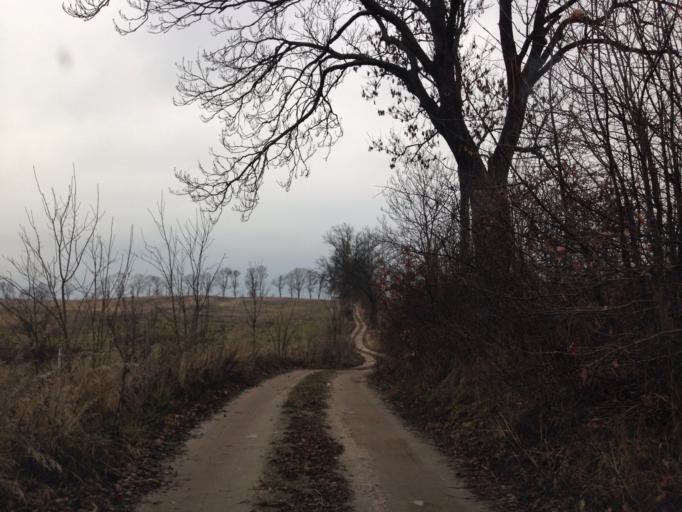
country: PL
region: Warmian-Masurian Voivodeship
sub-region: Powiat ketrzynski
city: Reszel
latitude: 54.0937
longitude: 21.1296
